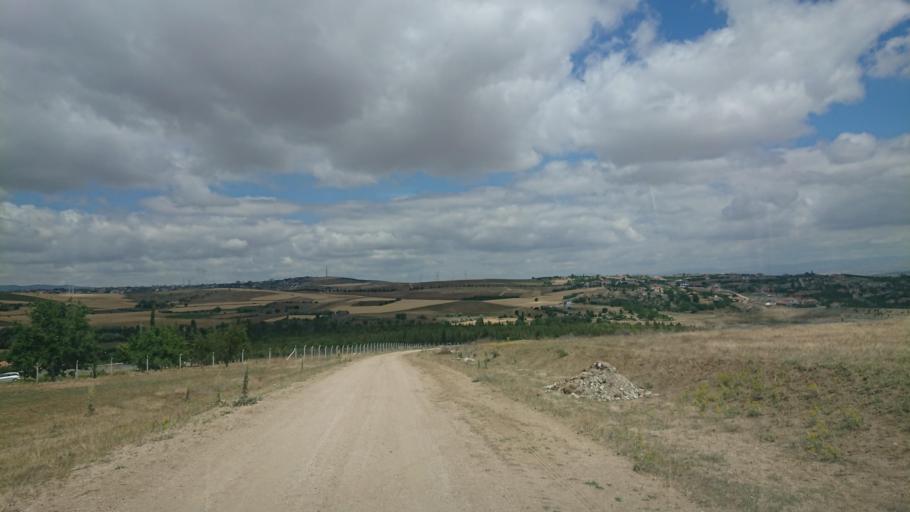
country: TR
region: Aksaray
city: Agacoren
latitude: 38.8576
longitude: 33.9490
